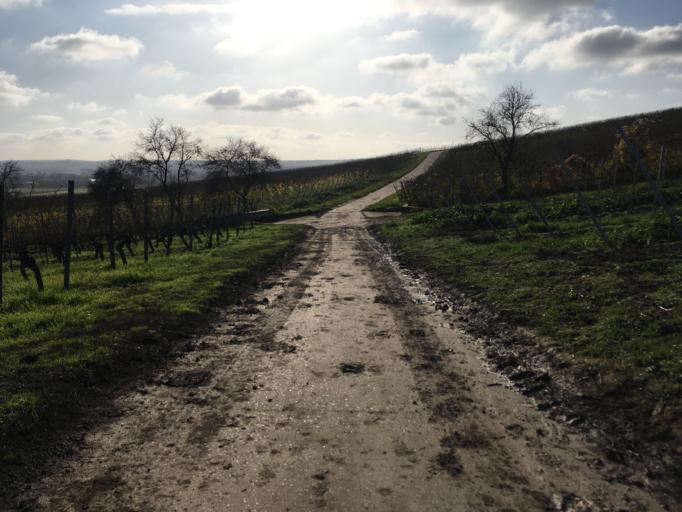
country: DE
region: Rheinland-Pfalz
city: Bodenheim
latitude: 49.9481
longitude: 8.3033
